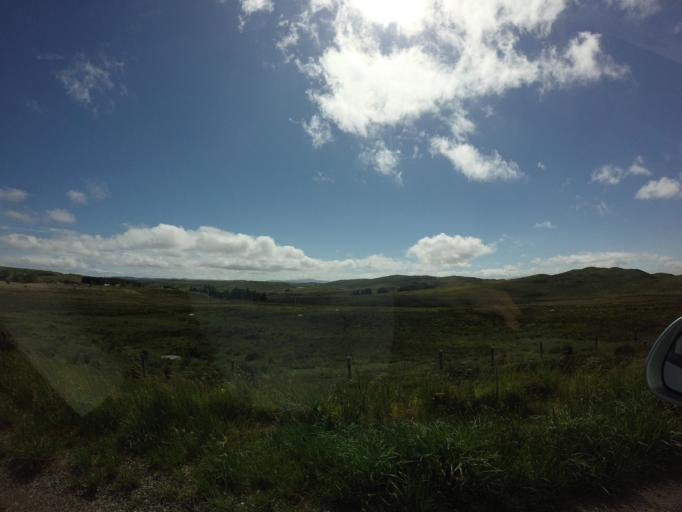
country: GB
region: Scotland
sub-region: Eilean Siar
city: Stornoway
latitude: 58.1548
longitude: -6.5051
